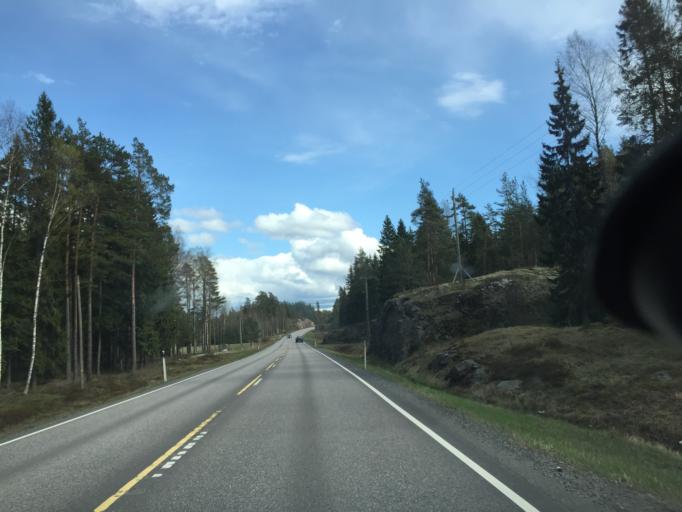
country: FI
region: Uusimaa
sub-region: Raaseporin
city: Ekenaes
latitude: 60.0396
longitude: 23.3486
